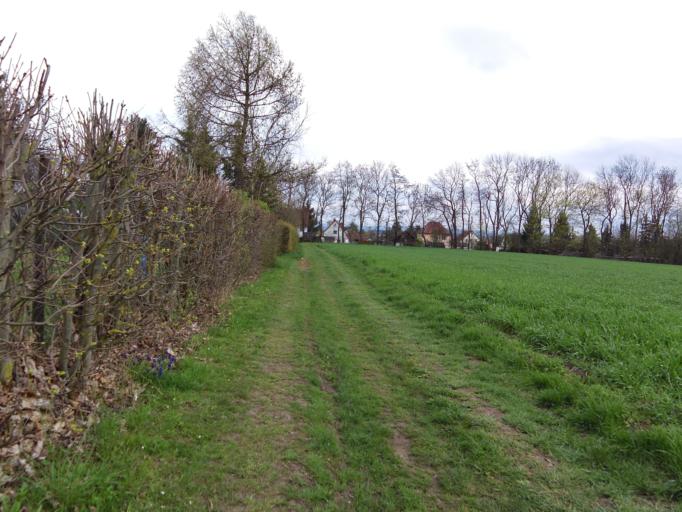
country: DE
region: Thuringia
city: Gotha
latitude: 50.9356
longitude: 10.6721
